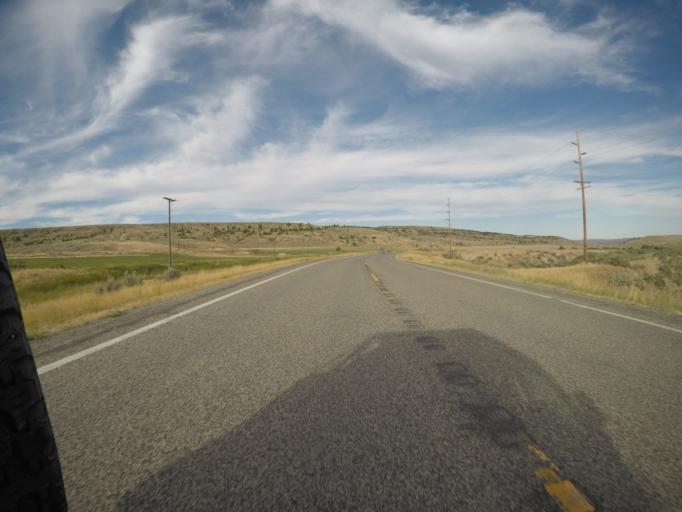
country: US
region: Montana
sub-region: Carbon County
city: Red Lodge
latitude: 45.1655
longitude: -109.1116
